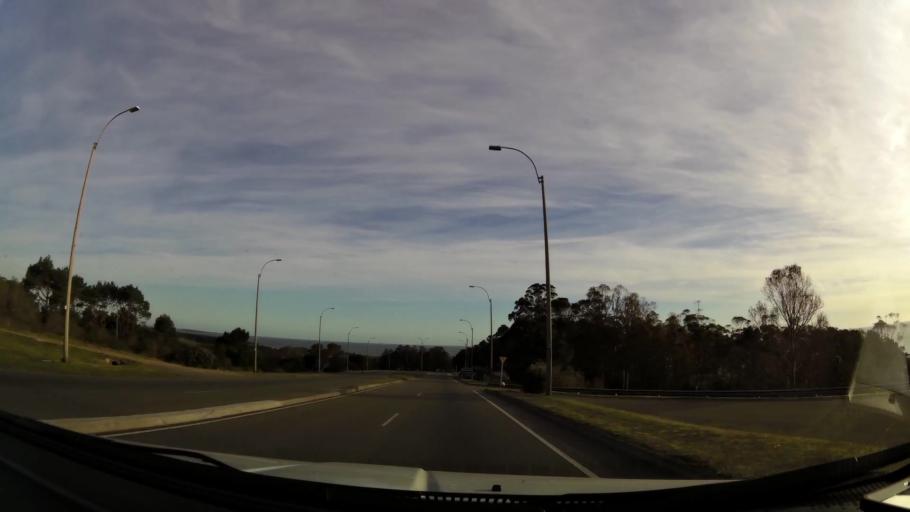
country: UY
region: Maldonado
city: Maldonado
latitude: -34.8960
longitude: -55.0382
